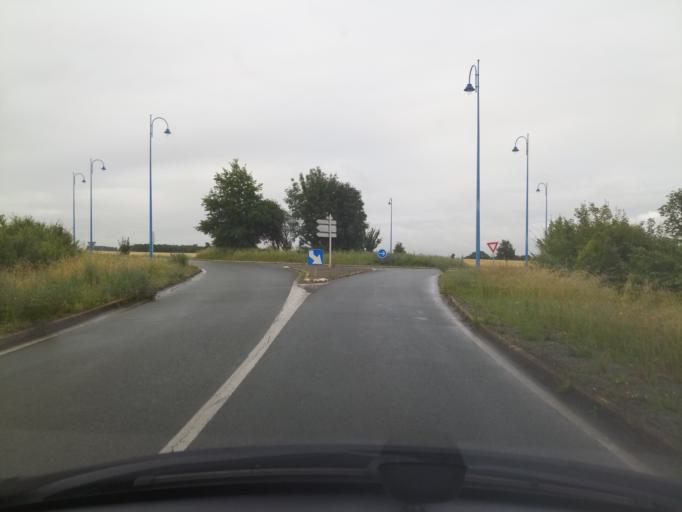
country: FR
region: Poitou-Charentes
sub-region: Departement de la Charente-Maritime
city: Courcon
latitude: 46.1832
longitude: -0.8551
